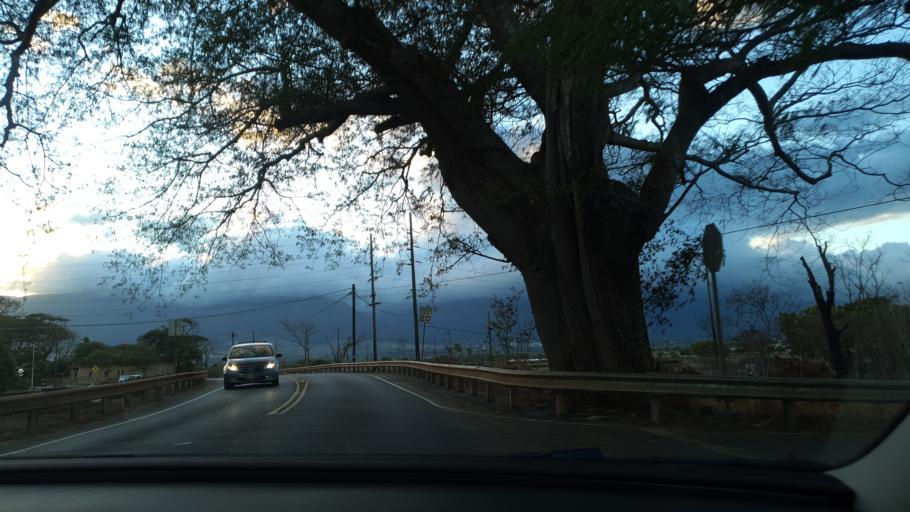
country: US
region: Hawaii
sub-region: Maui County
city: Kahului
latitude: 20.8699
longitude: -156.4529
